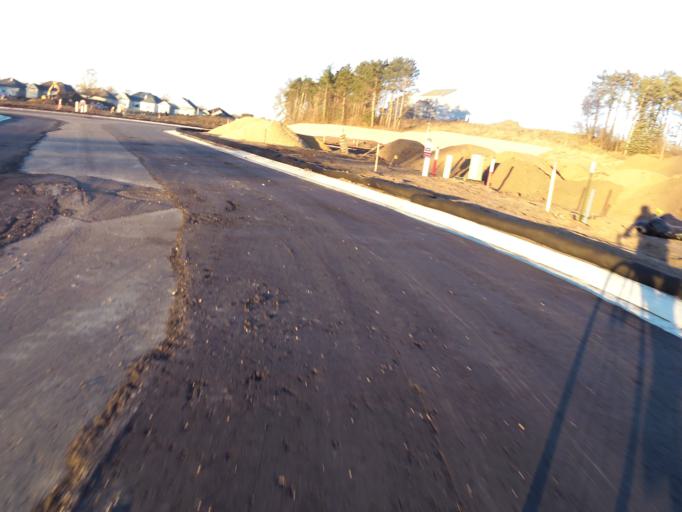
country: US
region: Wisconsin
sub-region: Saint Croix County
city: Hudson
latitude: 44.9656
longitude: -92.7298
